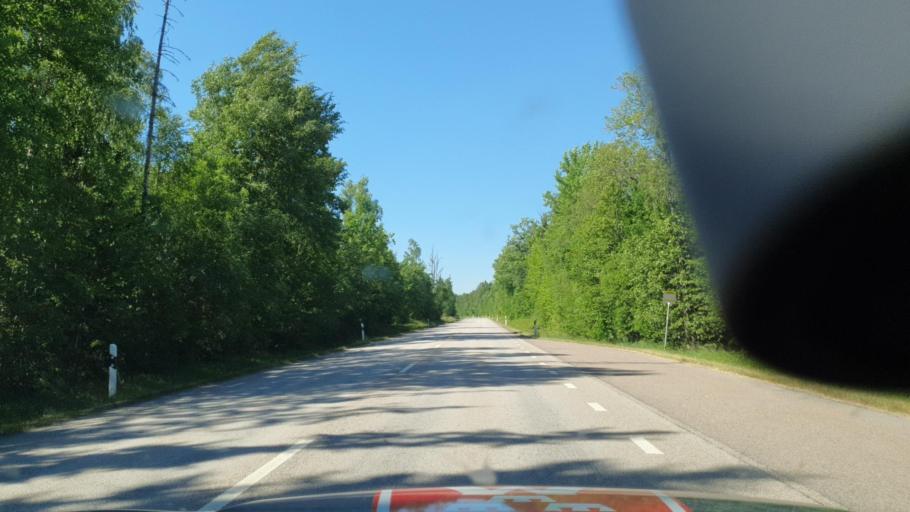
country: SE
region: Kalmar
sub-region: Emmaboda Kommun
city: Emmaboda
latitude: 56.6010
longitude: 15.5662
